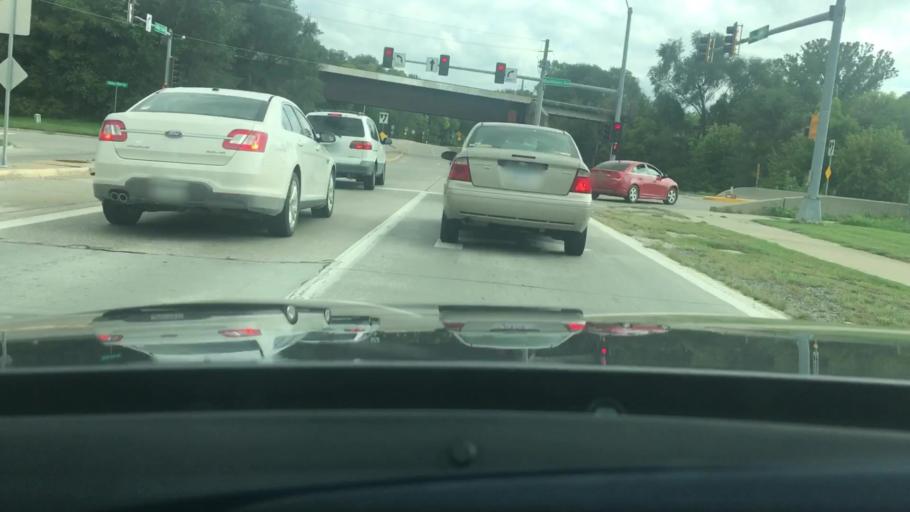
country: US
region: Iowa
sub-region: Pottawattamie County
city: Council Bluffs
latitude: 41.2426
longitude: -95.8184
